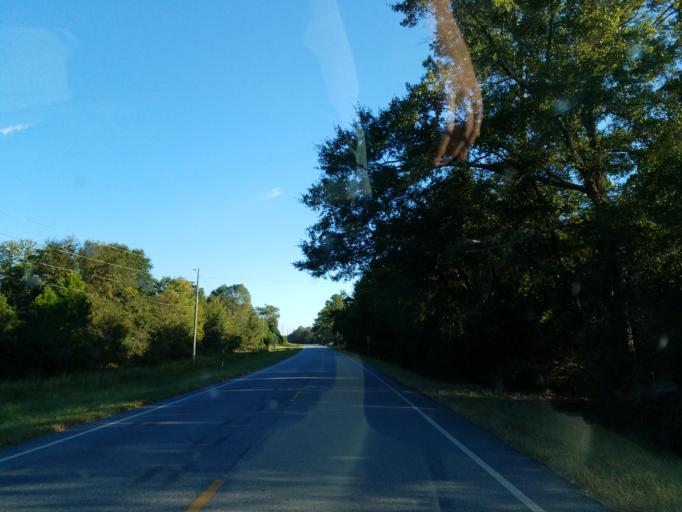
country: US
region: Georgia
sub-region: Worth County
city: Sylvester
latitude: 31.6958
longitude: -83.8850
